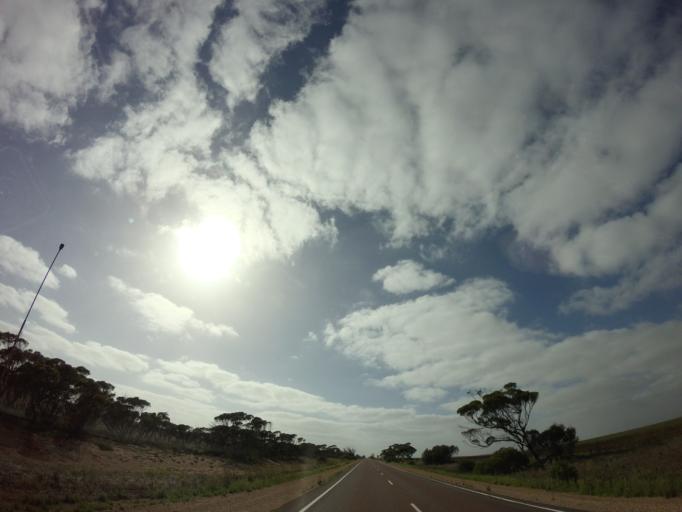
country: AU
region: South Australia
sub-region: Streaky Bay
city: Streaky Bay
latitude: -32.2849
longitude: 134.2288
